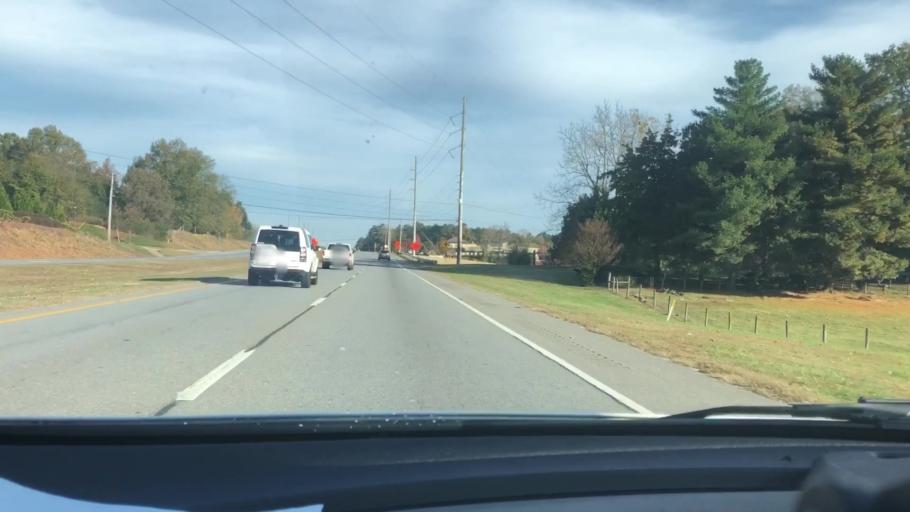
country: US
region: Georgia
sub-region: Fulton County
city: Johns Creek
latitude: 34.1018
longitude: -84.1769
